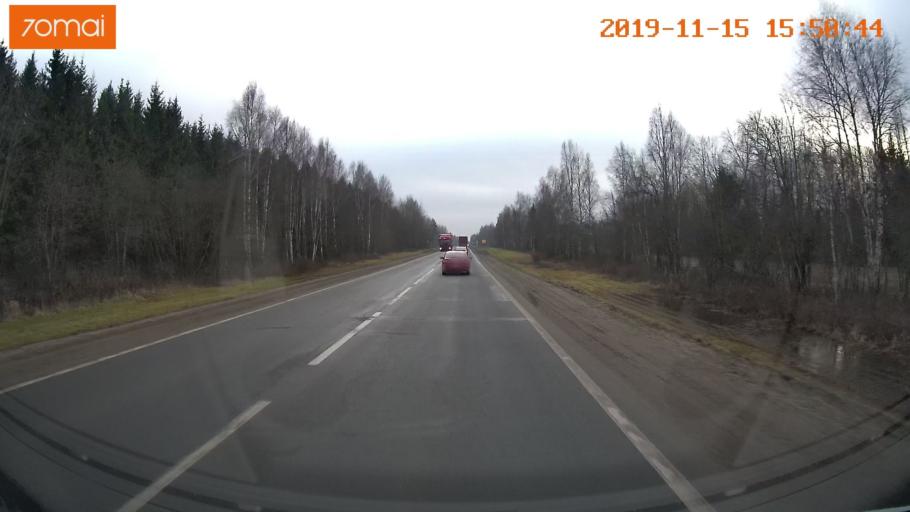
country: RU
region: Jaroslavl
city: Yaroslavl
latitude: 57.9024
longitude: 40.0124
